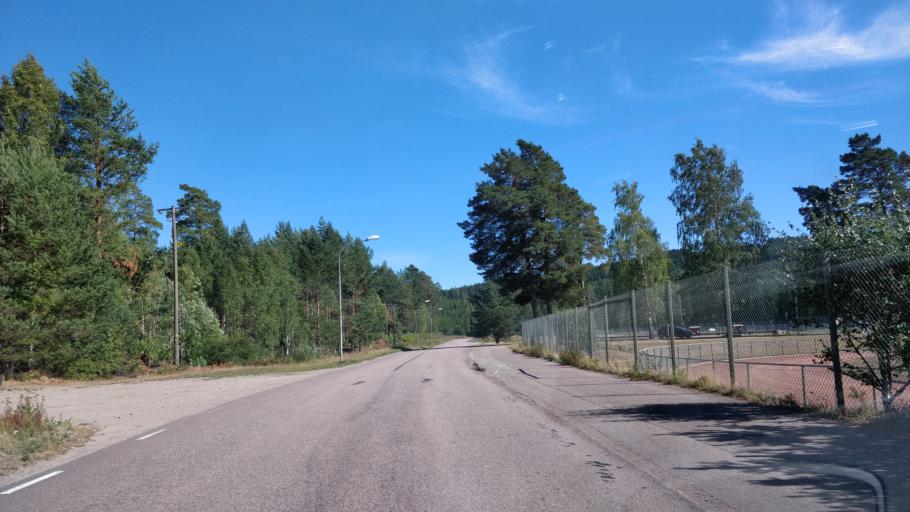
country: SE
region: Vaermland
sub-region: Hagfors Kommun
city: Hagfors
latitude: 60.0405
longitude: 13.7162
